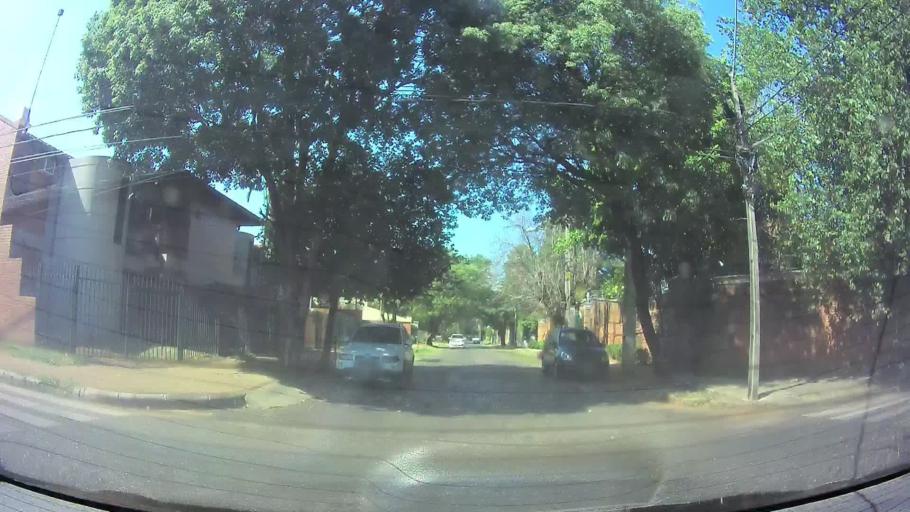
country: PY
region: Central
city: Fernando de la Mora
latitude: -25.2899
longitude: -57.5636
